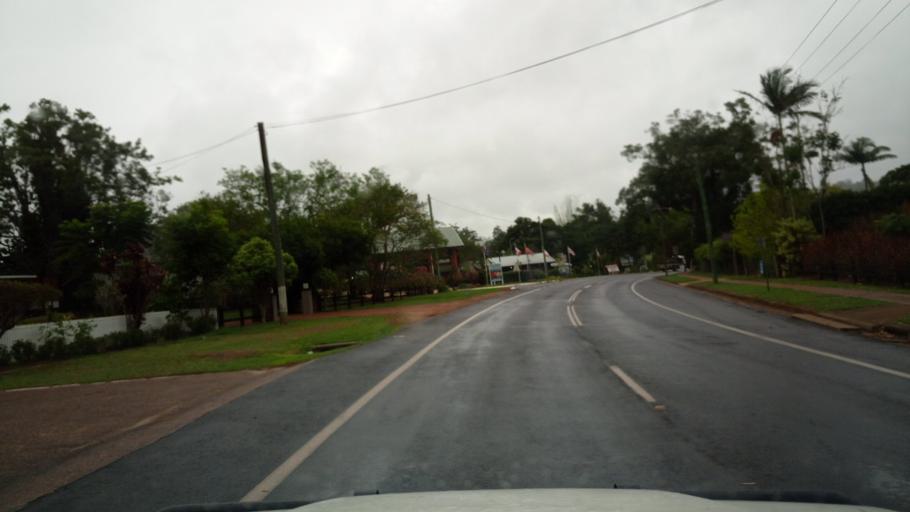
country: AU
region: Queensland
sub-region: Tablelands
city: Tolga
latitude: -17.2728
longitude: 145.5825
